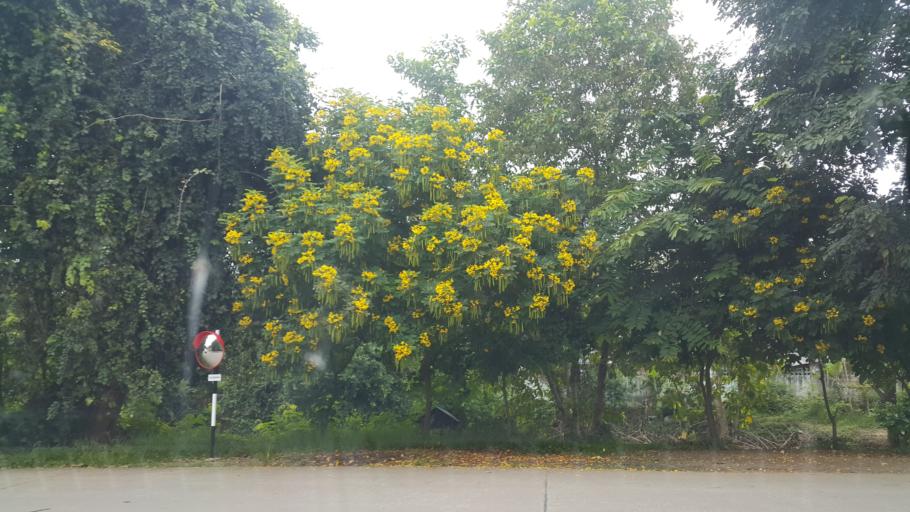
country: TH
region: Chiang Mai
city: San Kamphaeng
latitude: 18.7389
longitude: 99.0754
